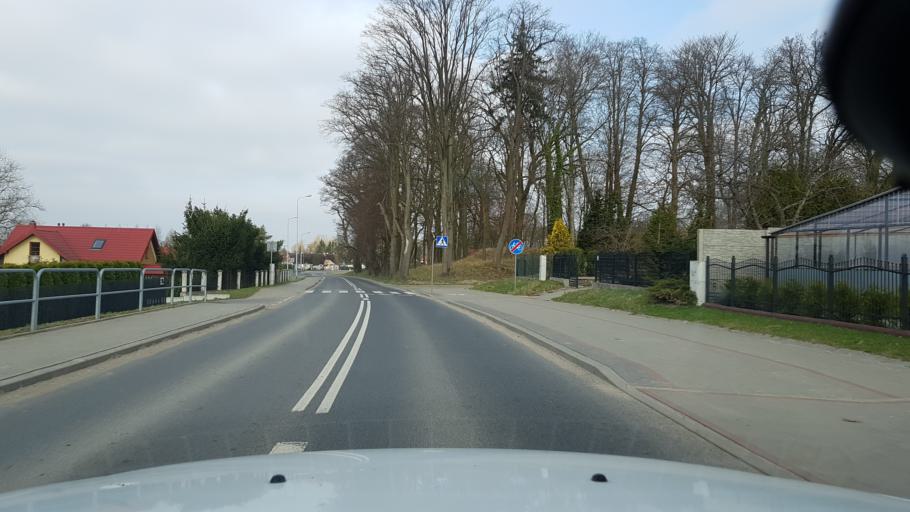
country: PL
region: West Pomeranian Voivodeship
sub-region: Powiat koszalinski
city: Sianow
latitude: 54.2583
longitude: 16.2711
